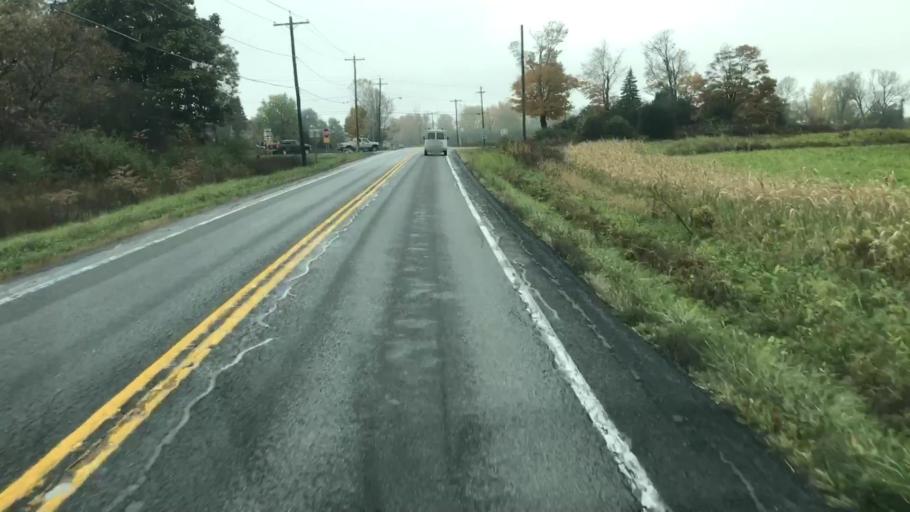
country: US
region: New York
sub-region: Onondaga County
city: Skaneateles
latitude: 42.9735
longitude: -76.4273
